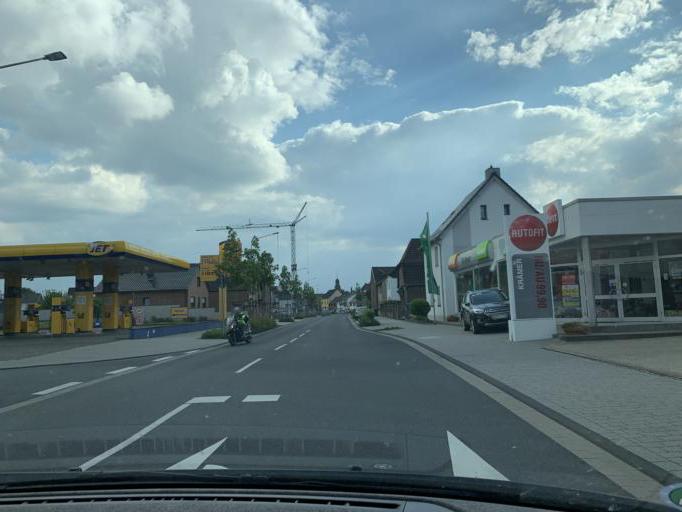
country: DE
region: North Rhine-Westphalia
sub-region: Regierungsbezirk Koln
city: Weilerswist
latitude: 50.7618
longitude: 6.8438
